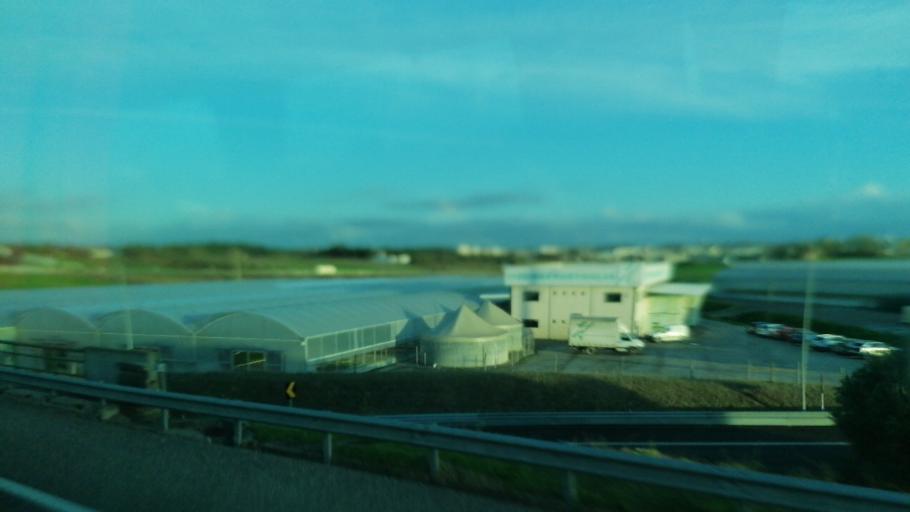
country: PT
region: Santarem
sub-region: Santarem
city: Santarem
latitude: 39.2670
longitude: -8.7254
